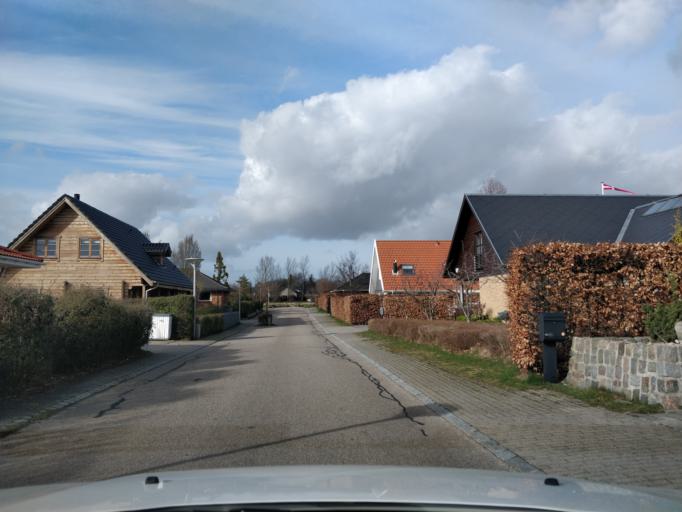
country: DK
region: Capital Region
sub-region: Hoje-Taastrup Kommune
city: Taastrup
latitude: 55.6488
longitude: 12.2526
